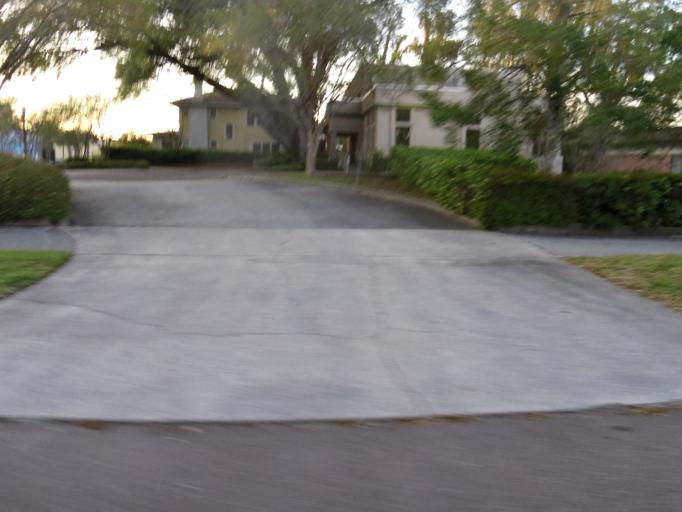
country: US
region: Florida
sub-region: Duval County
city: Jacksonville
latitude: 30.3092
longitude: -81.6923
